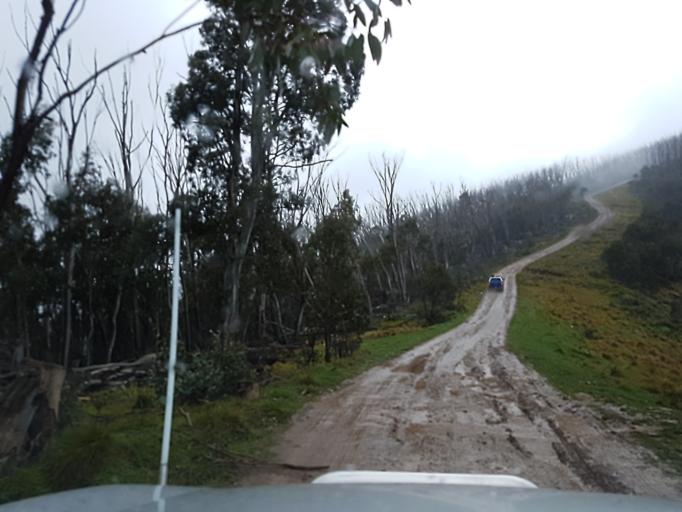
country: AU
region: Victoria
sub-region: Alpine
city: Mount Beauty
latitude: -37.0907
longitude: 147.0984
